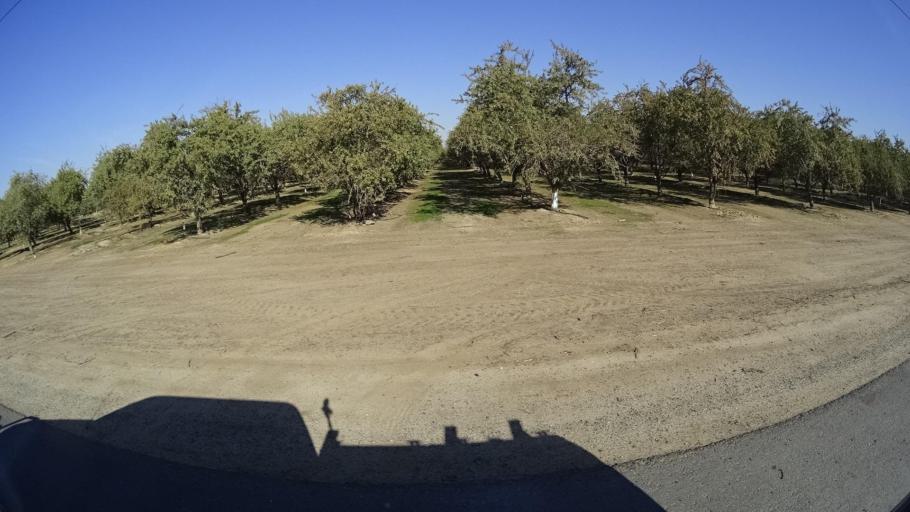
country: US
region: California
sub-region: Kern County
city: Delano
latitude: 35.7178
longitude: -119.3177
